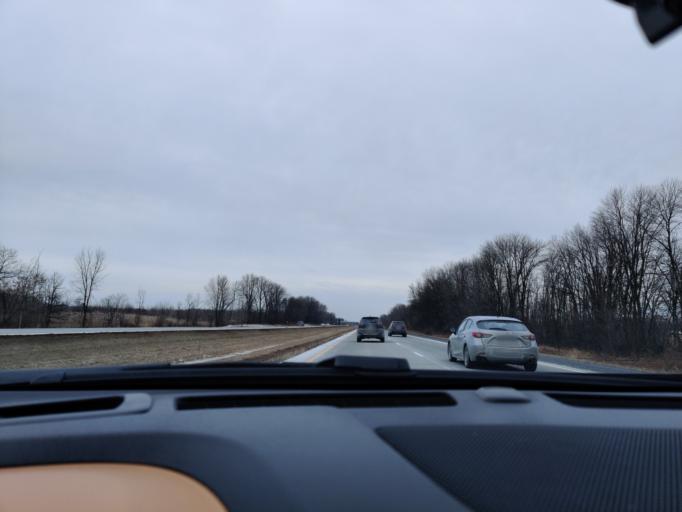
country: US
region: New York
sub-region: St. Lawrence County
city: Massena
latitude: 45.0390
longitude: -74.9284
